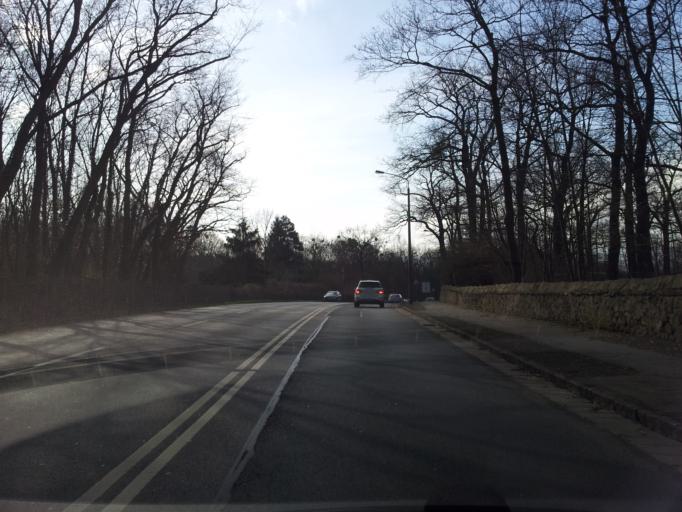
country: DE
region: Saxony
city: Albertstadt
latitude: 51.0912
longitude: 13.7378
